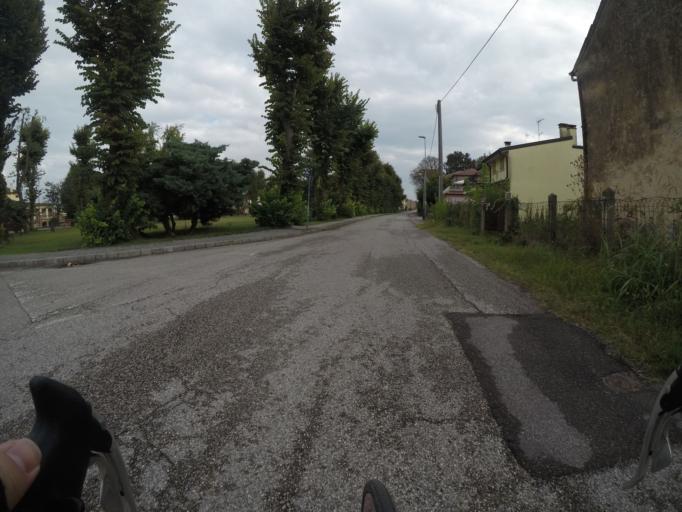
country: IT
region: Veneto
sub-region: Provincia di Rovigo
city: Polesella
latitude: 44.9639
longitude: 11.7495
